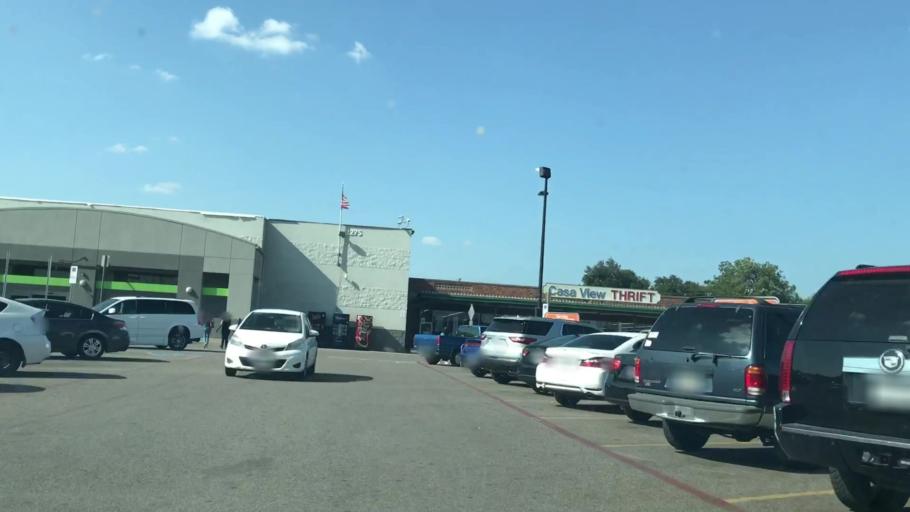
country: US
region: Texas
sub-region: Dallas County
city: Garland
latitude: 32.8352
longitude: -96.6760
